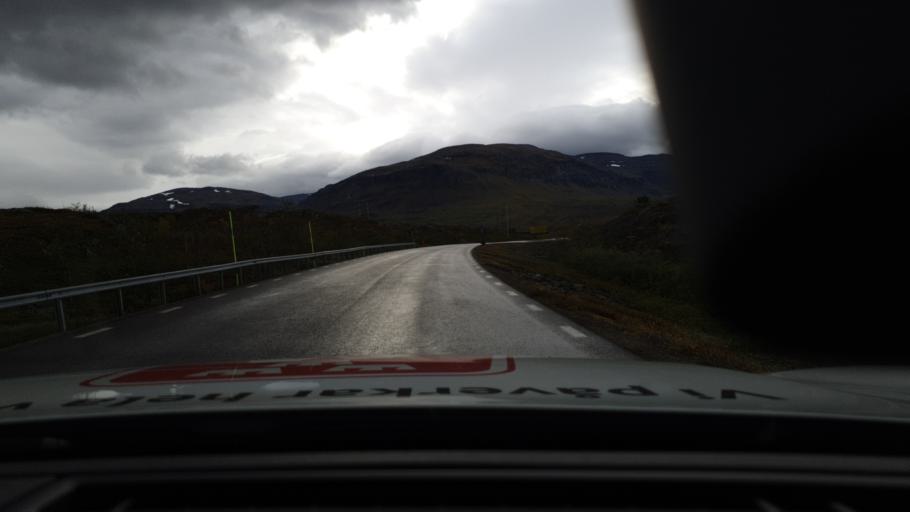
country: NO
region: Troms
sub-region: Bardu
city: Setermoen
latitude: 68.4335
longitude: 18.2601
